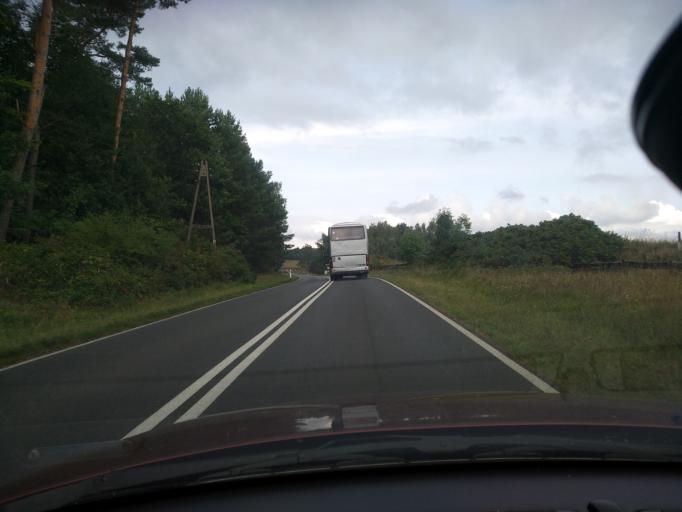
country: PL
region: West Pomeranian Voivodeship
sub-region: Powiat kamienski
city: Wolin
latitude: 53.9685
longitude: 14.6037
